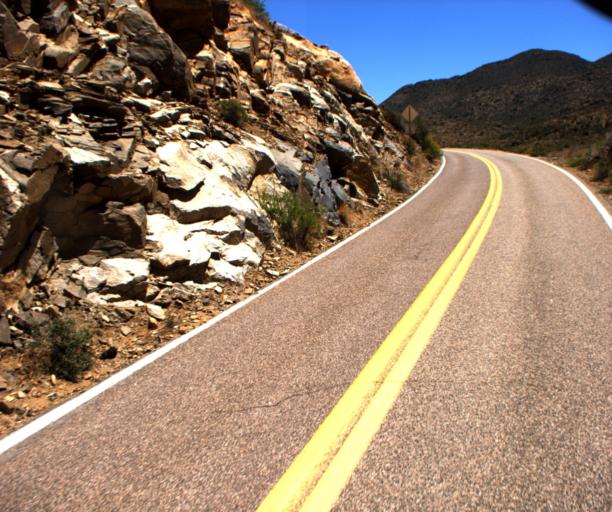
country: US
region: Arizona
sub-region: Yavapai County
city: Bagdad
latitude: 34.4490
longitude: -112.9728
